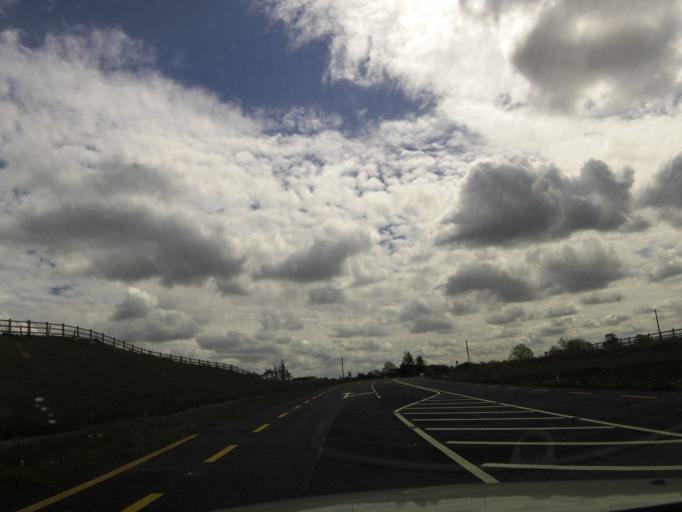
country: IE
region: Connaught
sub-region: County Galway
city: Tuam
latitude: 53.5714
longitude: -8.8409
